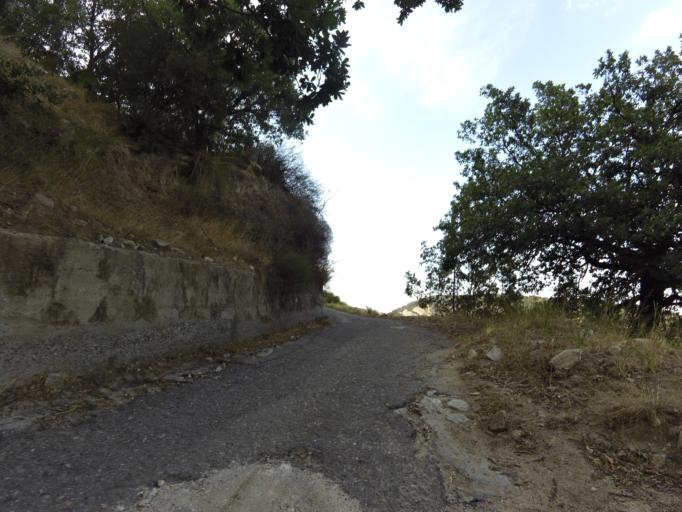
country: IT
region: Calabria
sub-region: Provincia di Reggio Calabria
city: Stilo
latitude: 38.4650
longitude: 16.4866
